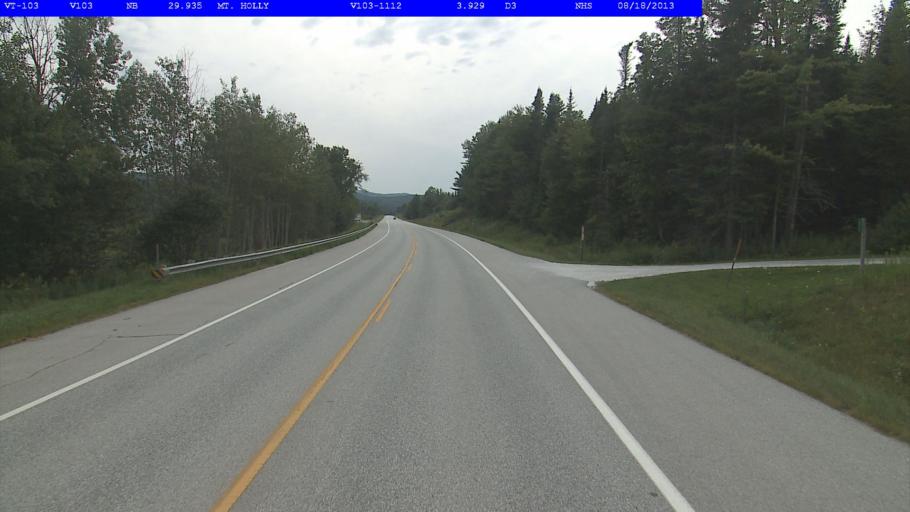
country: US
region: Vermont
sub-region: Rutland County
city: Rutland
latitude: 43.4555
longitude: -72.8021
